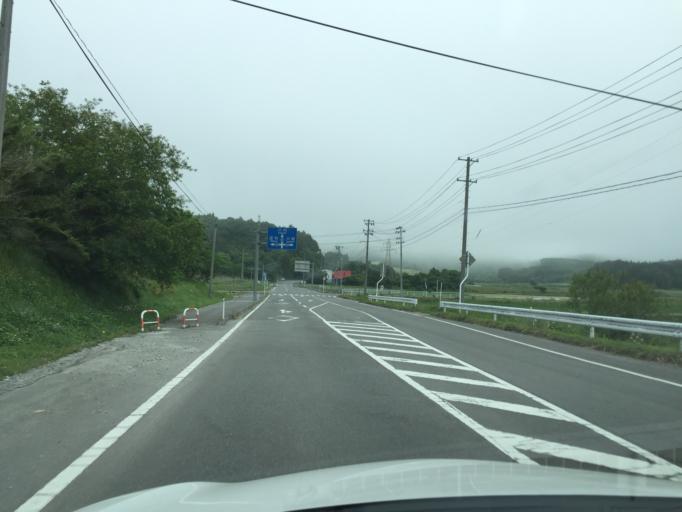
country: JP
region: Fukushima
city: Funehikimachi-funehiki
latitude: 37.2977
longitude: 140.7092
